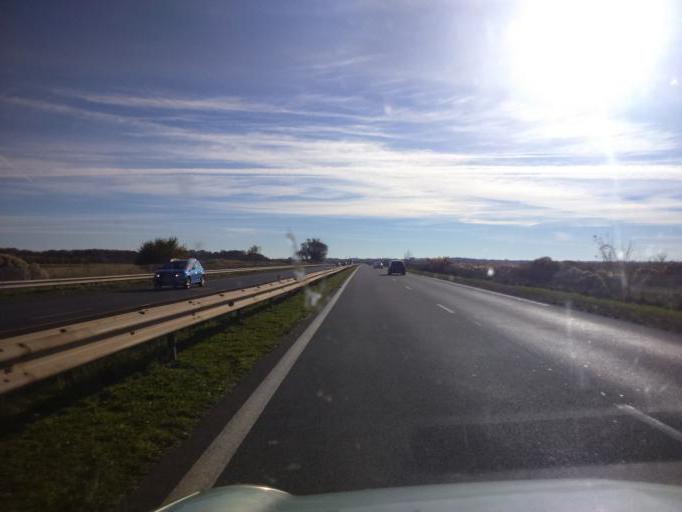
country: FR
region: Poitou-Charentes
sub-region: Departement de la Charente-Maritime
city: Saint-Laurent-de-la-Pree
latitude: 45.9846
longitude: -1.0238
